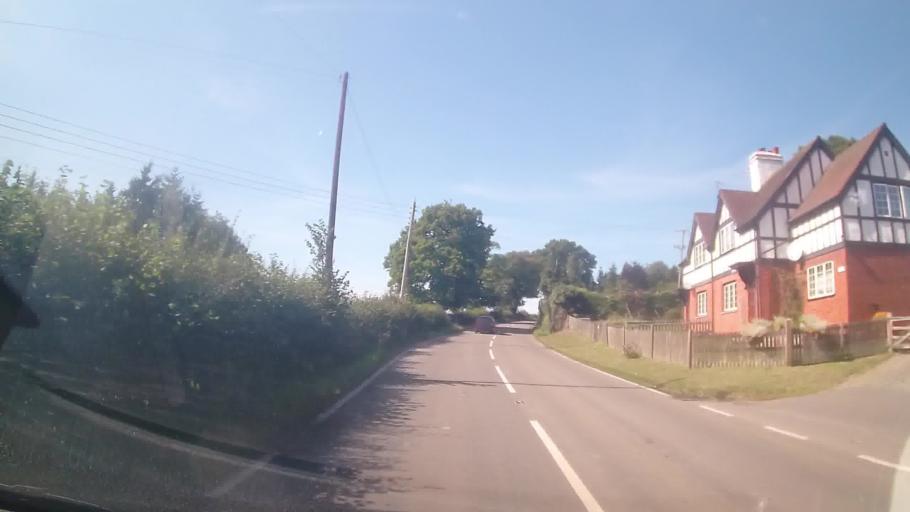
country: GB
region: England
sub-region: Shropshire
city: Lydham
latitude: 52.5207
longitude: -2.9945
